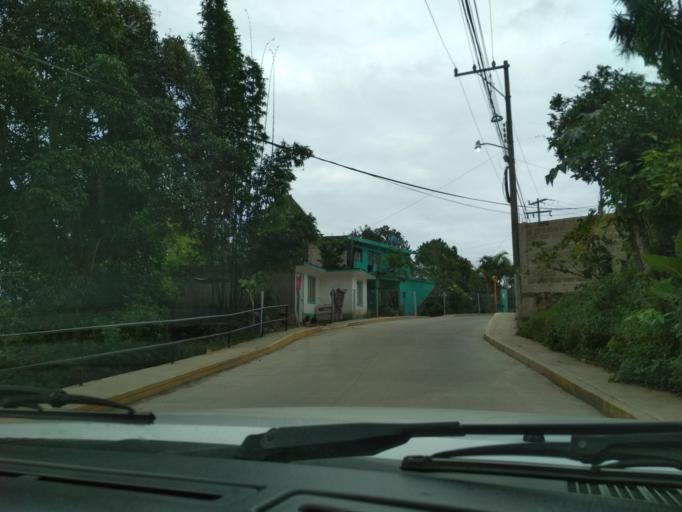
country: MX
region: Veracruz
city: El Castillo
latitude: 19.5849
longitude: -96.8730
